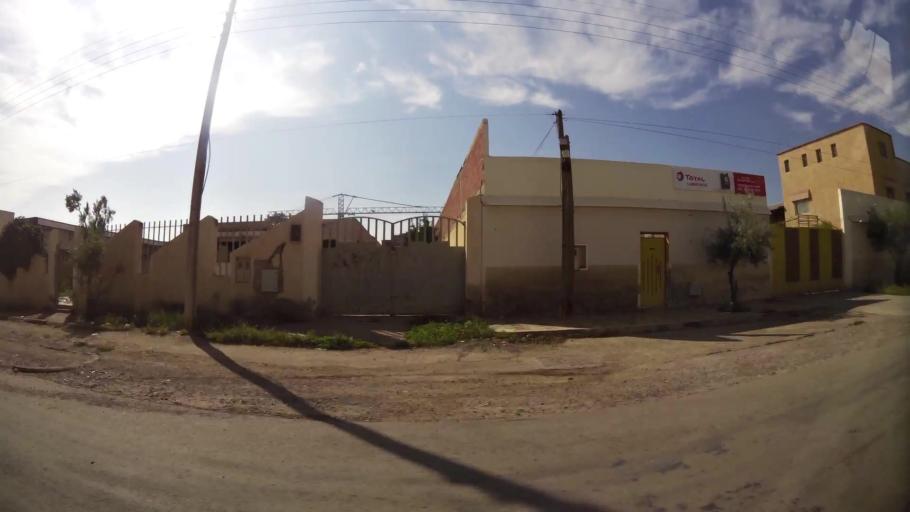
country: MA
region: Oriental
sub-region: Oujda-Angad
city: Oujda
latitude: 34.7084
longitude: -1.8891
